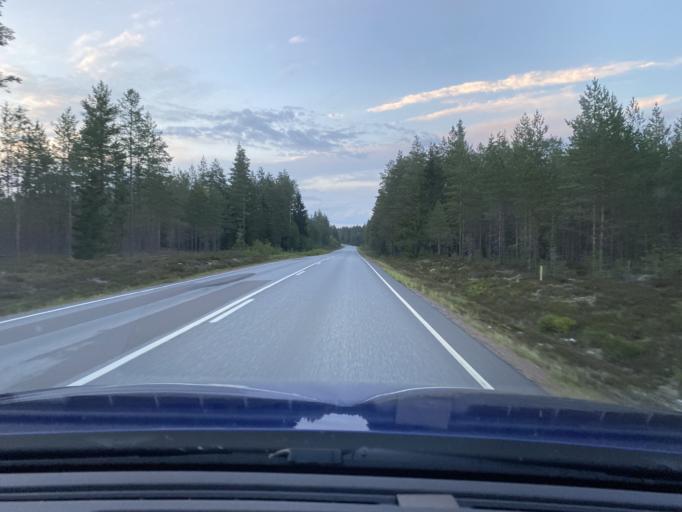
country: FI
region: Satakunta
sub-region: Pohjois-Satakunta
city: Honkajoki
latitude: 62.0330
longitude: 22.2373
